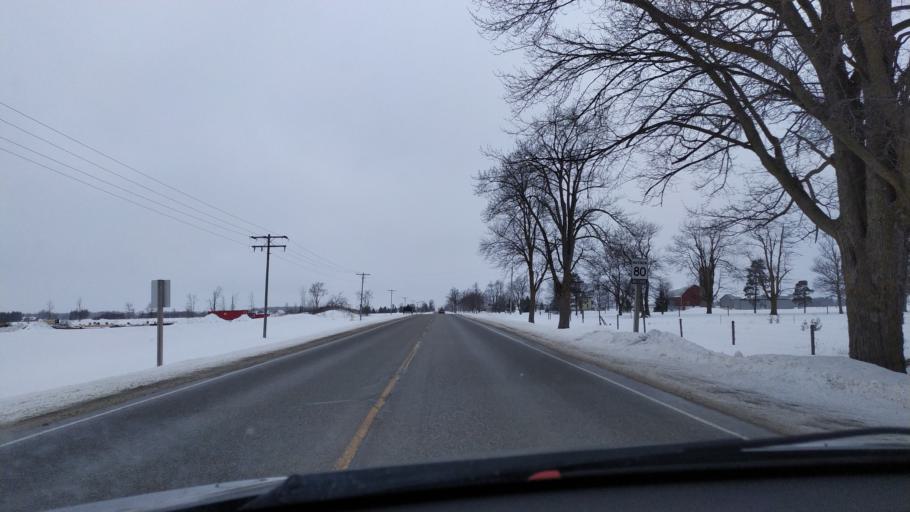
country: CA
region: Ontario
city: North Perth
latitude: 43.5911
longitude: -80.8813
